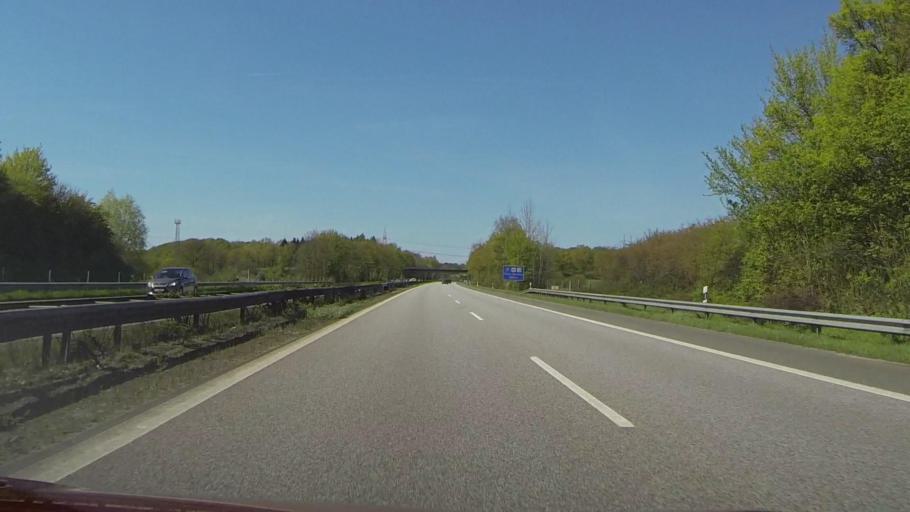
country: DE
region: Schleswig-Holstein
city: Kummerfeld
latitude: 53.6905
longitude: 9.7844
